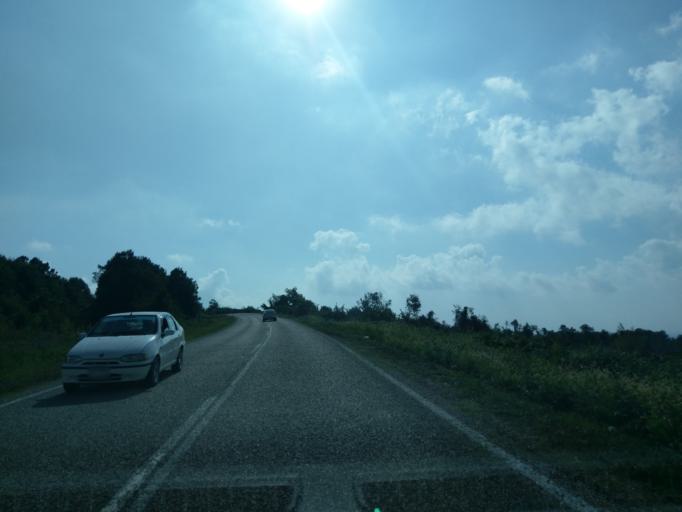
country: TR
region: Sinop
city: Erfelek
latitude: 41.9749
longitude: 34.8672
